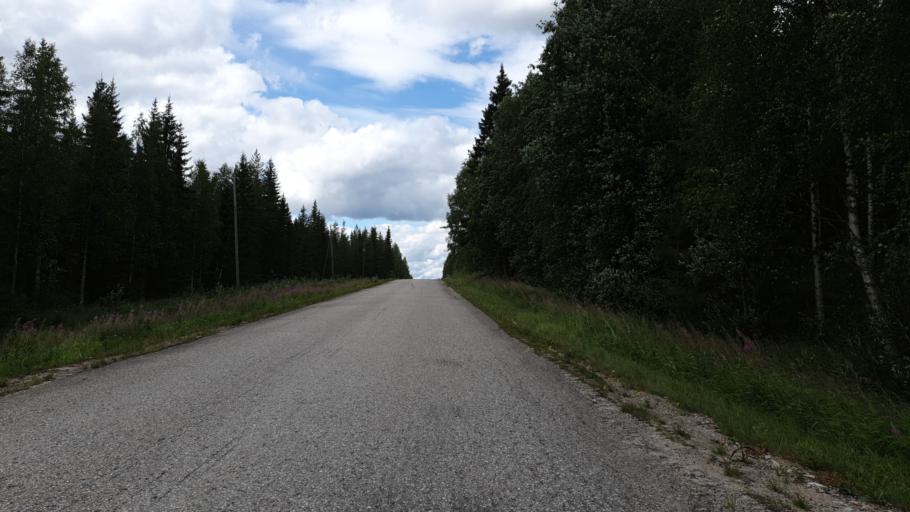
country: FI
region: Kainuu
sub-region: Kehys-Kainuu
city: Kuhmo
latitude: 64.4310
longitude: 29.7239
